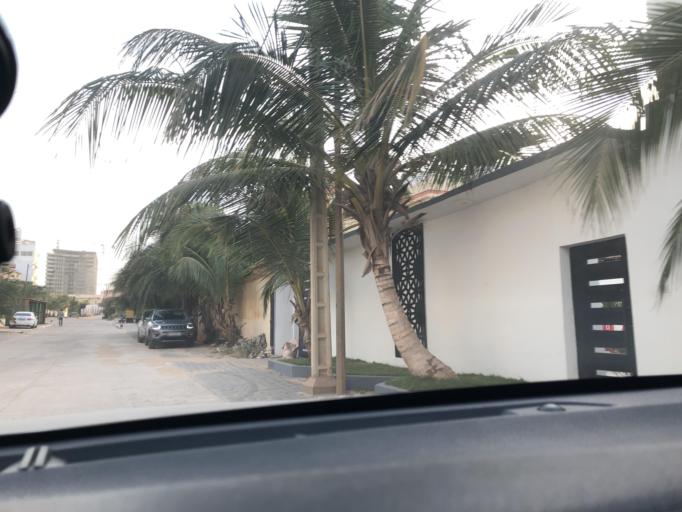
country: SN
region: Dakar
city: Mermoz Boabab
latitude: 14.7321
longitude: -17.5017
